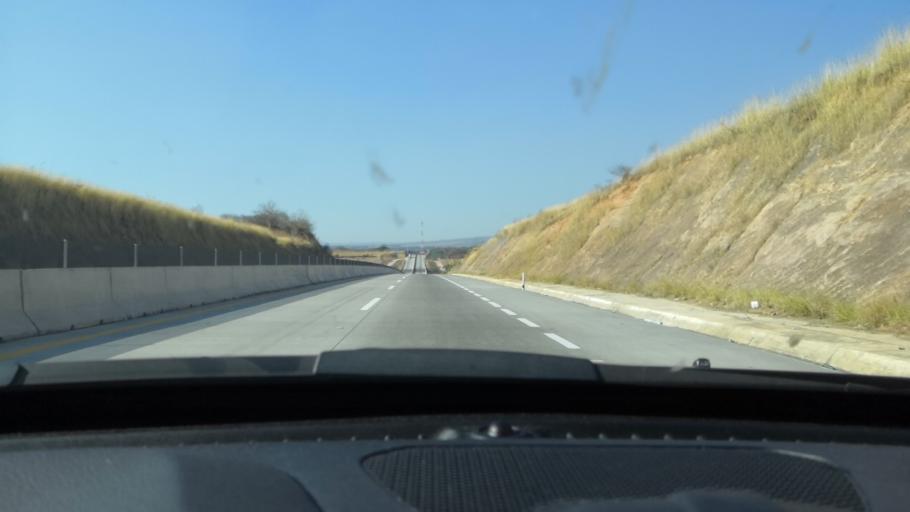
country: MX
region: Jalisco
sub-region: Zapotlanejo
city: La Mezquitera
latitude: 20.5935
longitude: -103.1000
